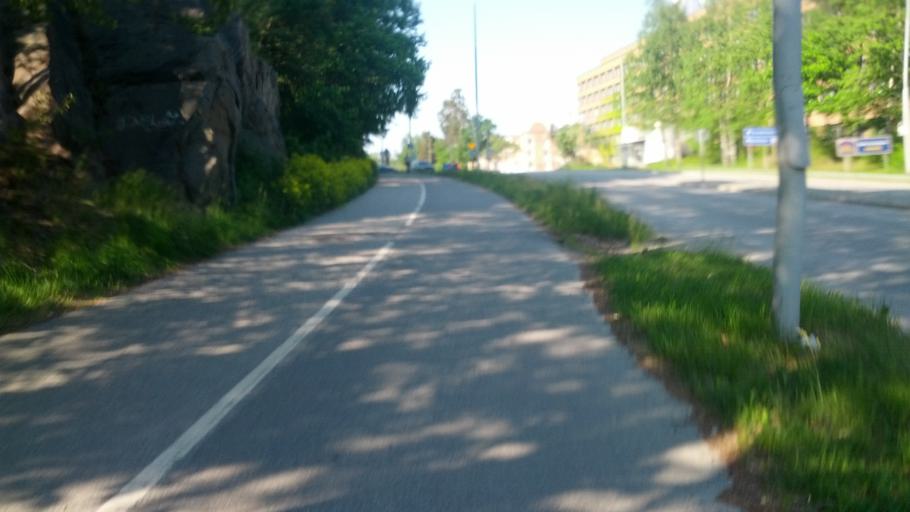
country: SE
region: Stockholm
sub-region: Danderyds Kommun
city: Djursholm
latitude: 59.3943
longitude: 18.0501
